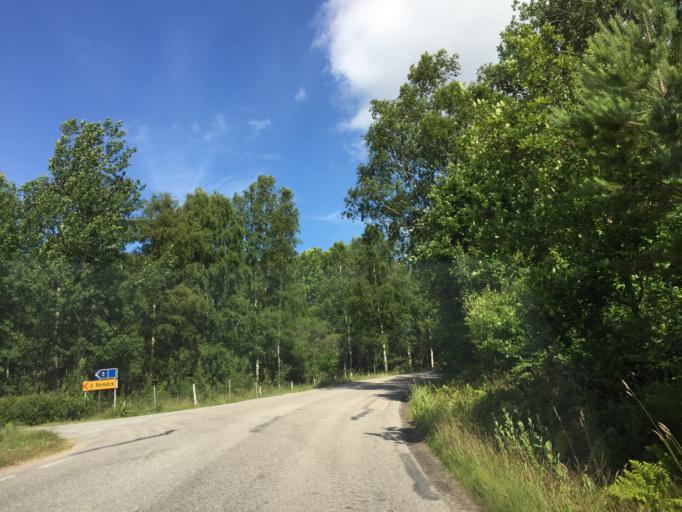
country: SE
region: Vaestra Goetaland
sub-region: Orust
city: Henan
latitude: 58.2843
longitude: 11.5824
